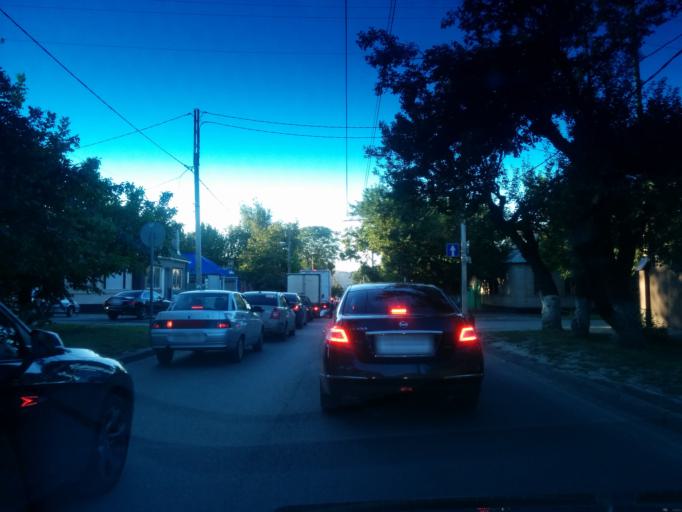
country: RU
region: Rostov
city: Severnyy
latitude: 47.2687
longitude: 39.7221
